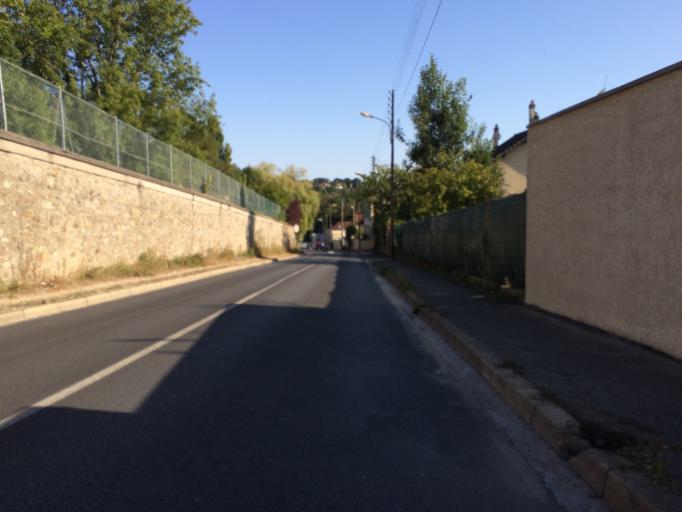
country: FR
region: Ile-de-France
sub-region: Departement de l'Essonne
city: Villiers-sur-Orge
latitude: 48.6588
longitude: 2.3072
